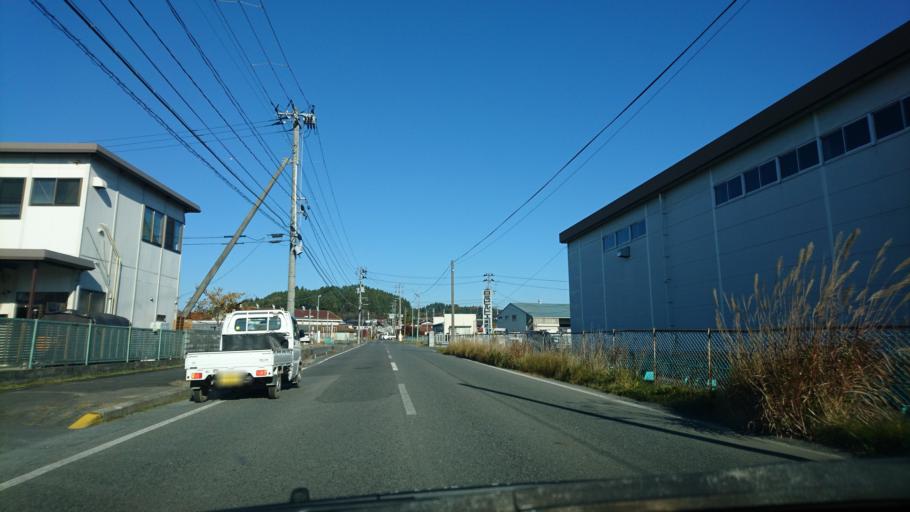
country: JP
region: Iwate
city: Mizusawa
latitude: 39.0386
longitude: 141.1227
